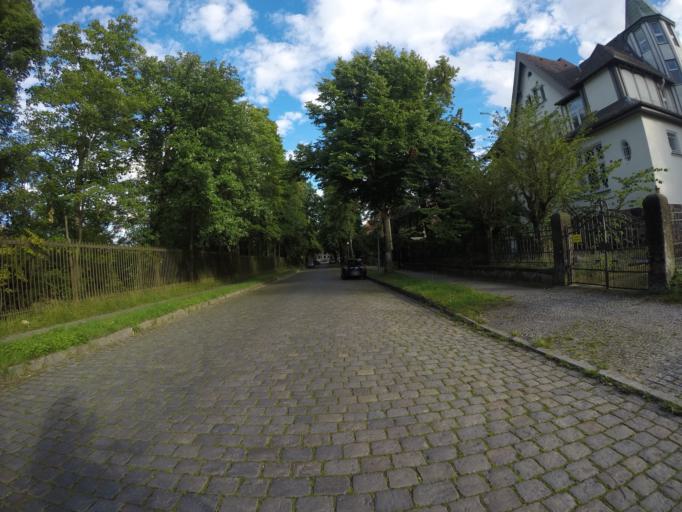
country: DE
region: Berlin
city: Lichterfelde
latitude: 52.4512
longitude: 13.3040
